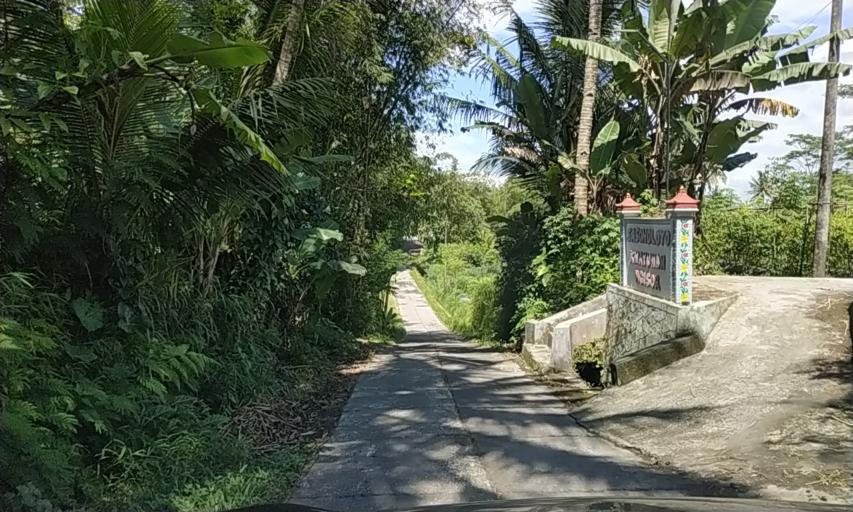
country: ID
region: Central Java
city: Muntilan
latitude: -7.5623
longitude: 110.3393
